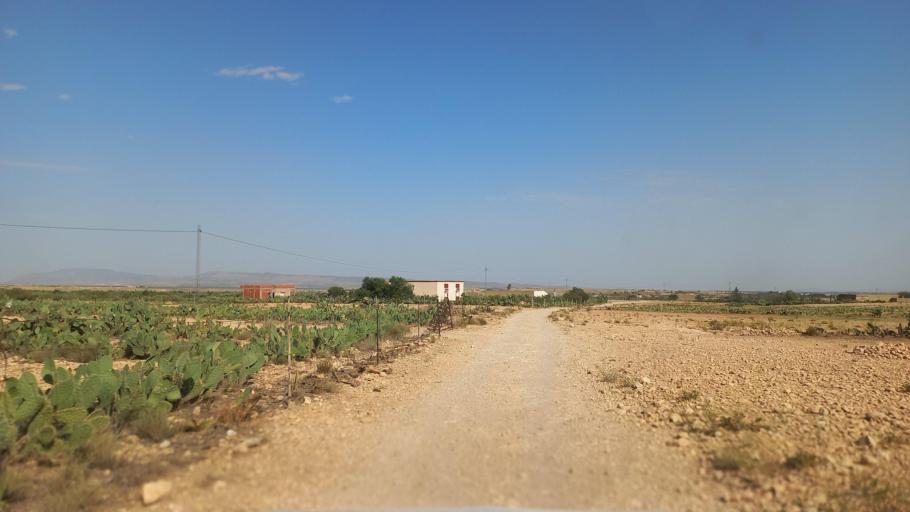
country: TN
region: Al Qasrayn
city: Kasserine
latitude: 35.2839
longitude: 8.9431
